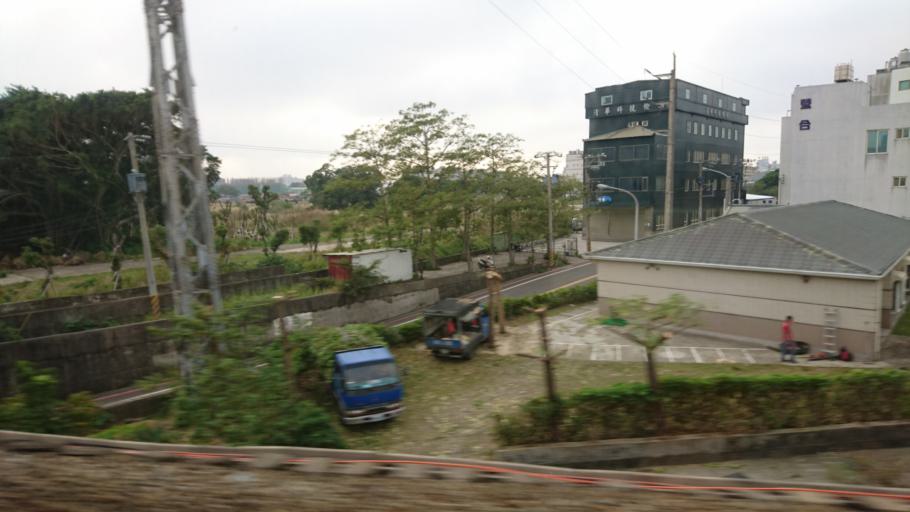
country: TW
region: Taiwan
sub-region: Hsinchu
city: Zhubei
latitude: 24.8462
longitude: 121.0137
